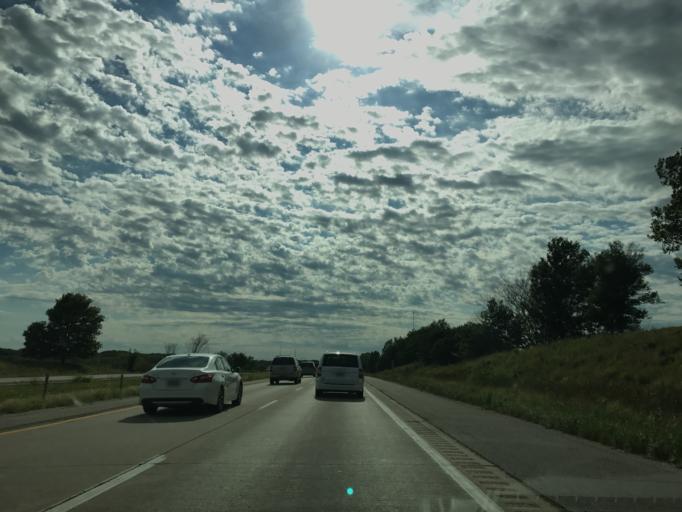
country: US
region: Iowa
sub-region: Dallas County
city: Waukee
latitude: 41.5590
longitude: -93.9012
